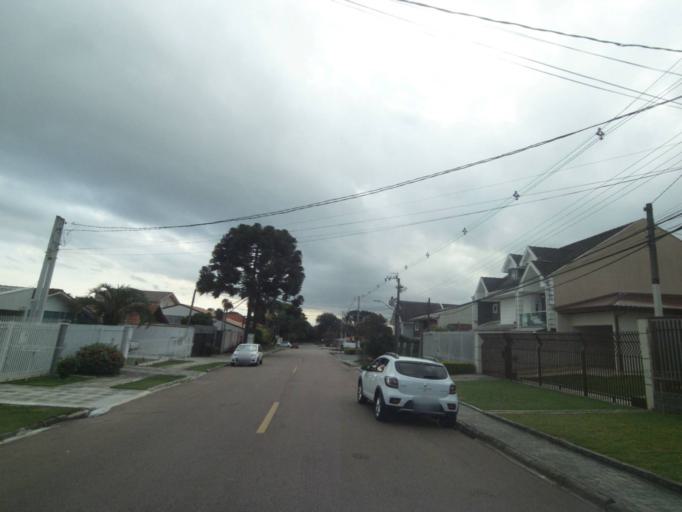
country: BR
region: Parana
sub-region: Pinhais
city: Pinhais
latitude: -25.4171
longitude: -49.2123
